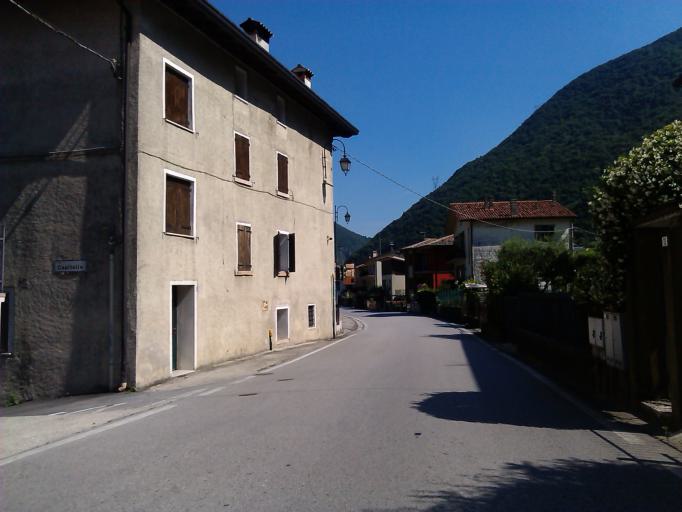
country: IT
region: Veneto
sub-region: Provincia di Vicenza
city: Campolongo sul Brenta
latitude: 45.8285
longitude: 11.7002
